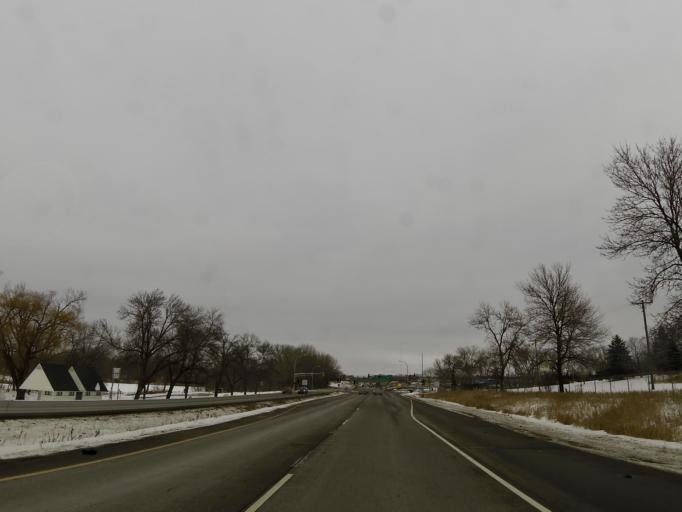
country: US
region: Minnesota
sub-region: Ramsey County
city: Little Canada
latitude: 45.0067
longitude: -93.0582
